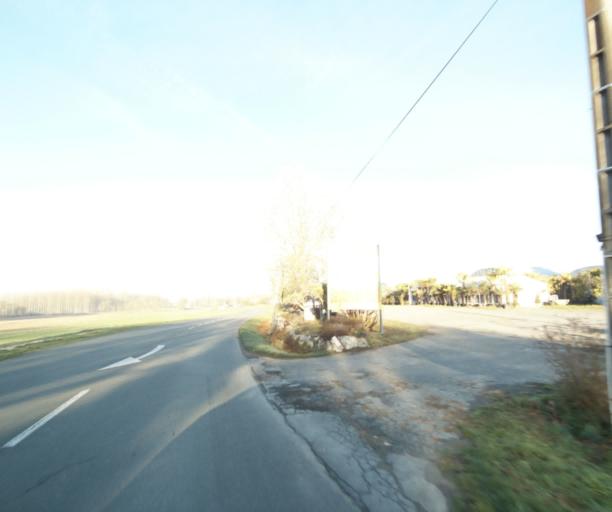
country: FR
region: Poitou-Charentes
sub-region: Departement de la Charente-Maritime
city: Cherac
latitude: 45.6951
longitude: -0.4784
